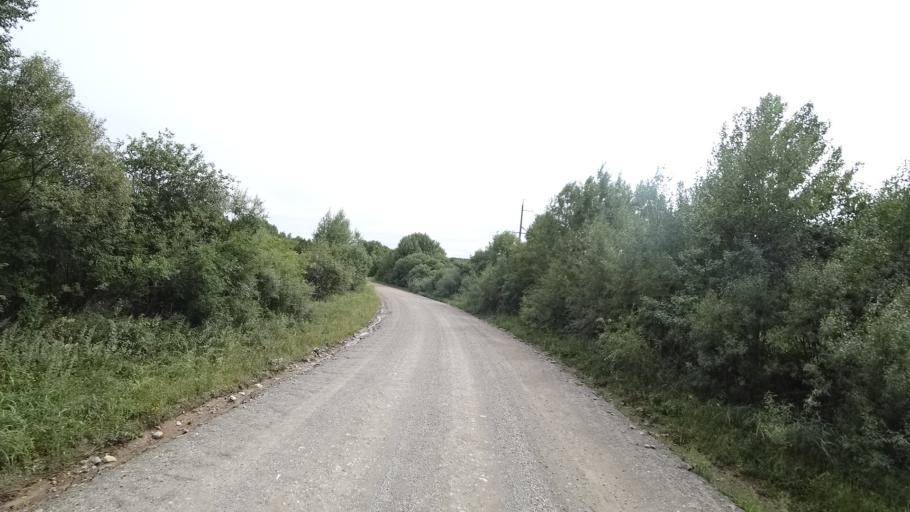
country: RU
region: Primorskiy
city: Lyalichi
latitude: 44.0889
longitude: 132.4349
